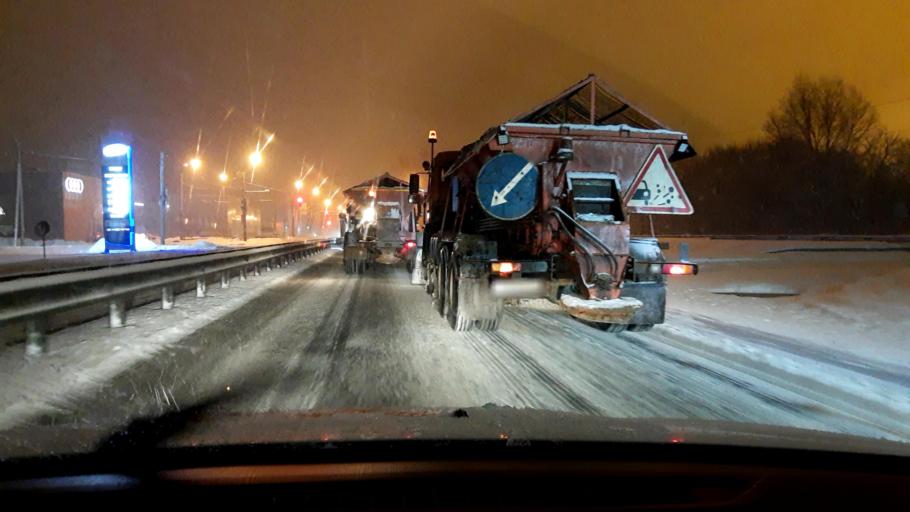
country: RU
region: Nizjnij Novgorod
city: Gorbatovka
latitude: 56.3099
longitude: 43.7991
